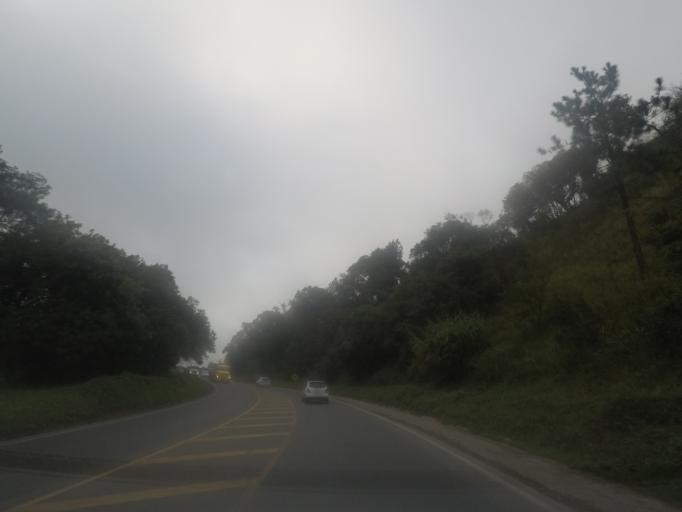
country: BR
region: Parana
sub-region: Almirante Tamandare
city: Almirante Tamandare
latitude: -25.2884
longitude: -49.3078
